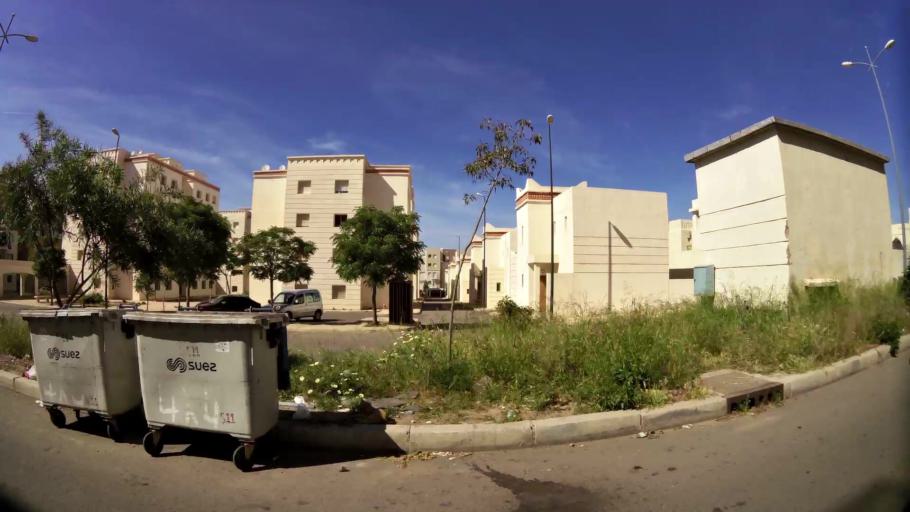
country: MA
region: Oriental
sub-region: Oujda-Angad
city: Oujda
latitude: 34.6610
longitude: -1.9178
